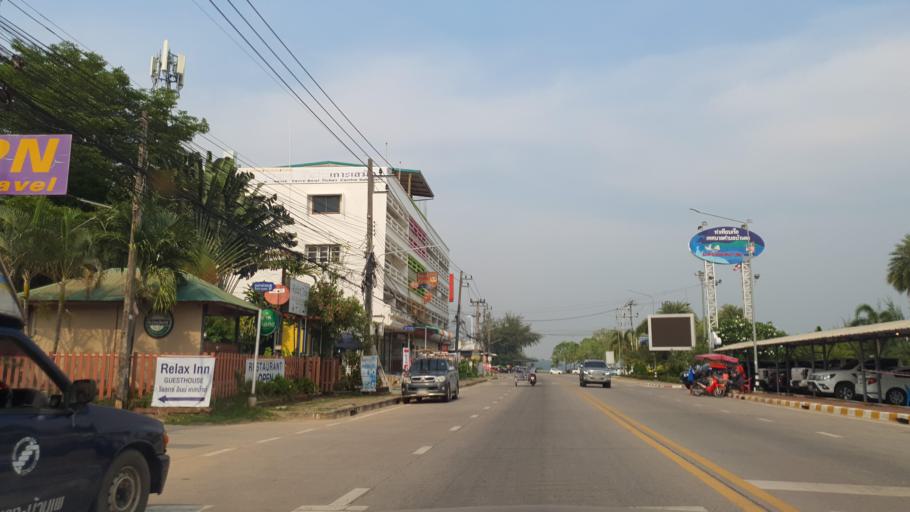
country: TH
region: Rayong
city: Rayong
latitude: 12.6286
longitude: 101.4427
